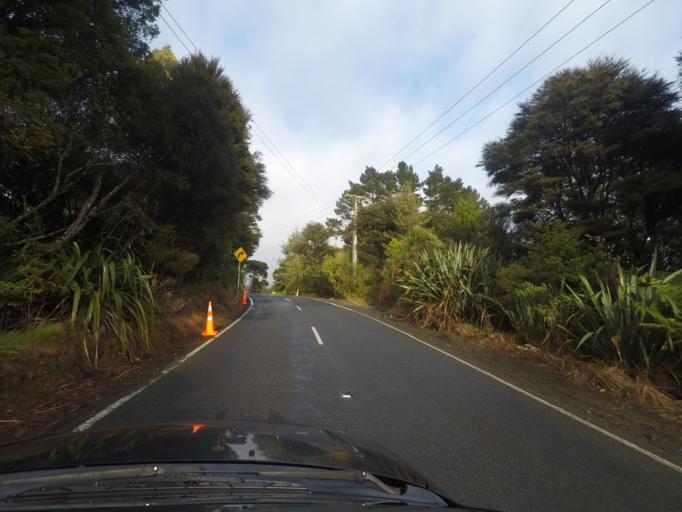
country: NZ
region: Auckland
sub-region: Auckland
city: Waitakere
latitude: -36.9166
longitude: 174.5973
